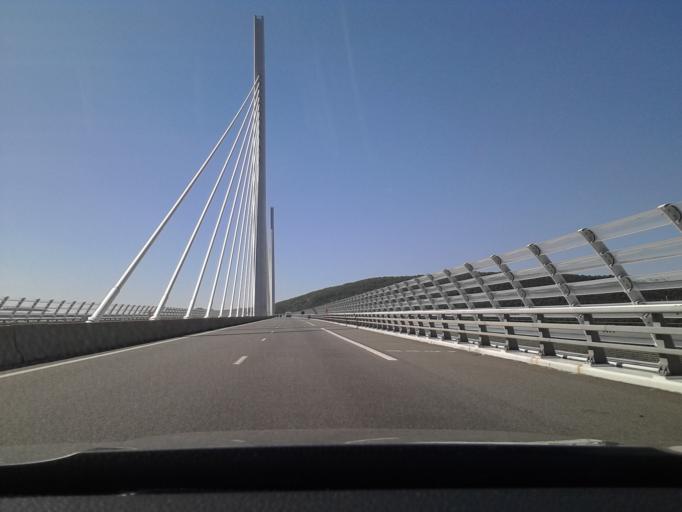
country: FR
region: Midi-Pyrenees
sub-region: Departement de l'Aveyron
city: Creissels
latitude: 44.0877
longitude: 3.0214
